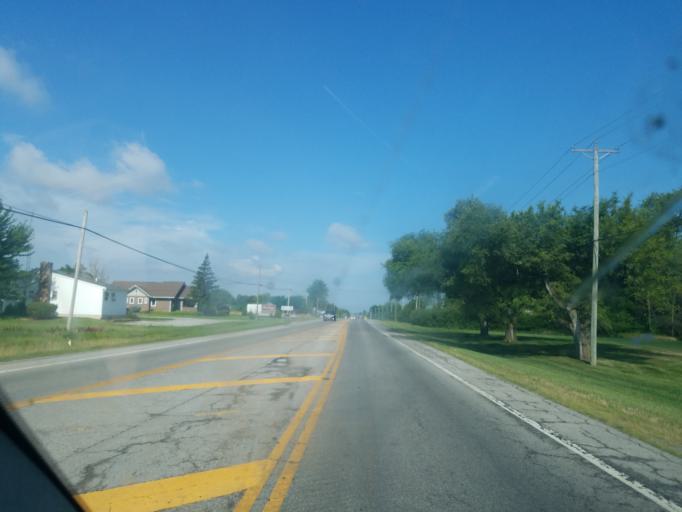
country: US
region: Ohio
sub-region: Allen County
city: Lima
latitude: 40.7312
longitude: -84.0247
